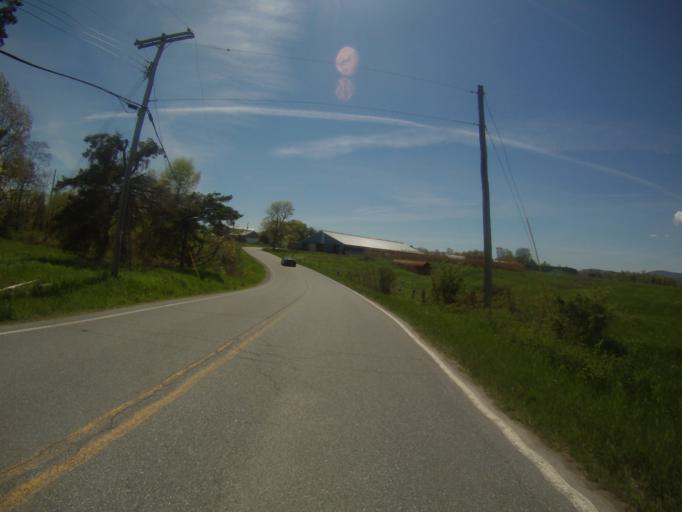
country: US
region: New York
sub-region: Essex County
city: Port Henry
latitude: 44.0007
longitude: -73.4176
